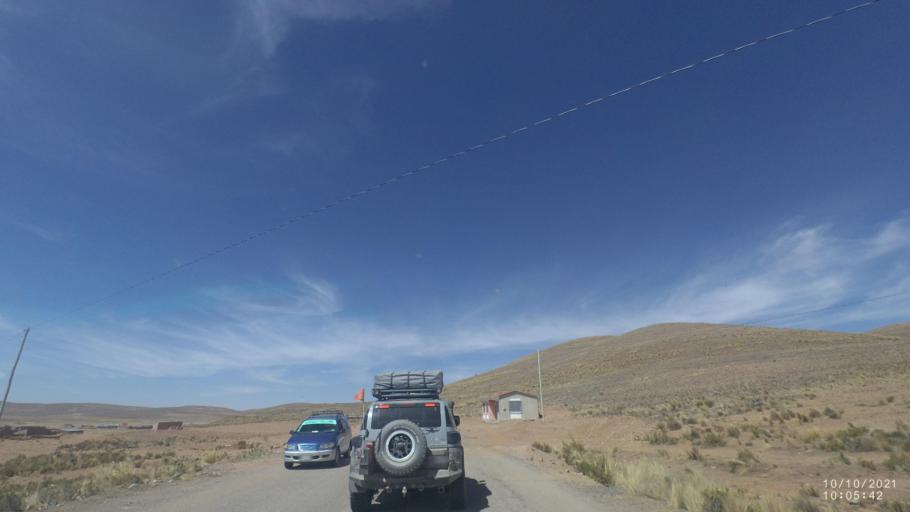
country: BO
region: La Paz
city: Eucaliptus
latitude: -17.3780
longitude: -67.4584
